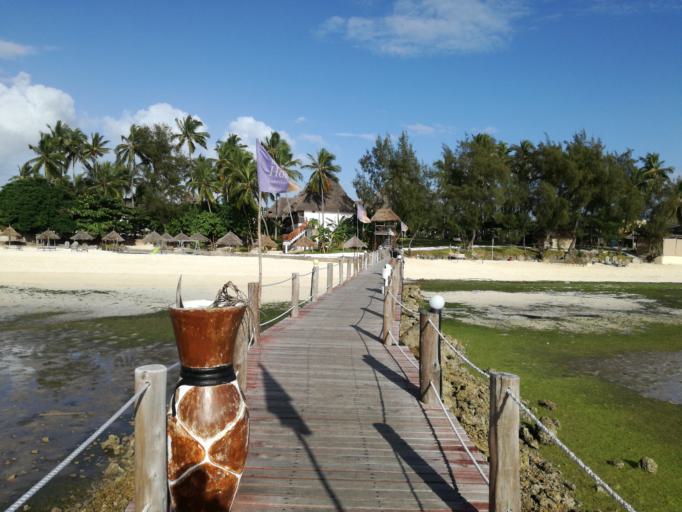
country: TZ
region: Zanzibar Central/South
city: Koani
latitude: -6.1355
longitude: 39.4263
